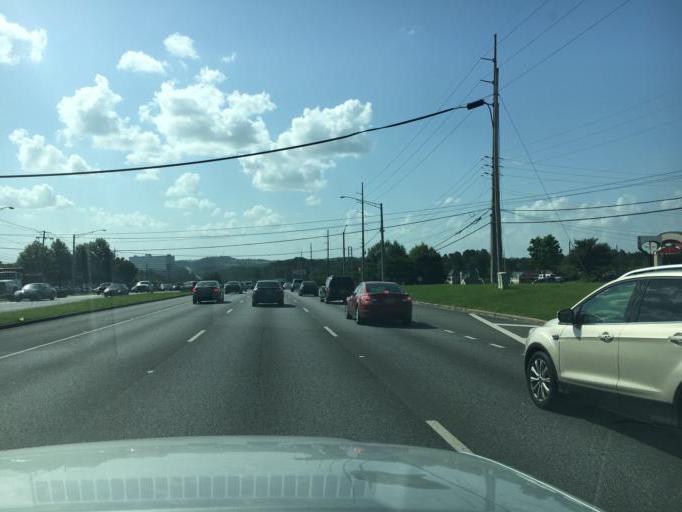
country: US
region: Alabama
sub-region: Shelby County
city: Lake Purdy
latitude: 33.4259
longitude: -86.7044
